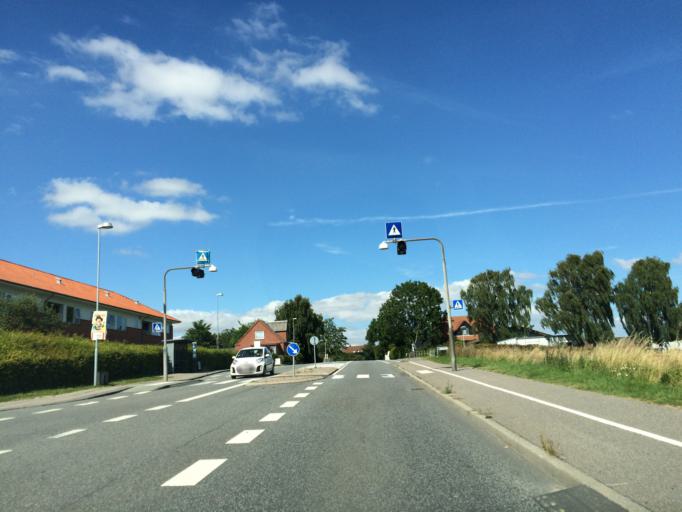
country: DK
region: Central Jutland
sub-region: Arhus Kommune
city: Logten
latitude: 56.2700
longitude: 10.3104
